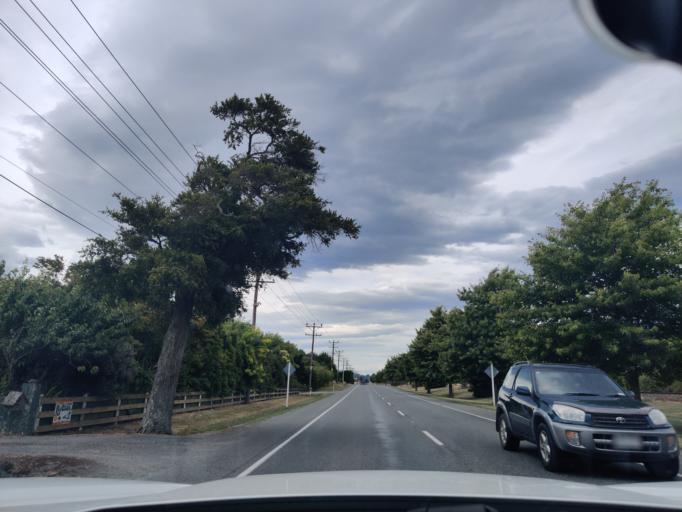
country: NZ
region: Wellington
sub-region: Masterton District
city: Masterton
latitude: -40.9576
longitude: 175.6155
